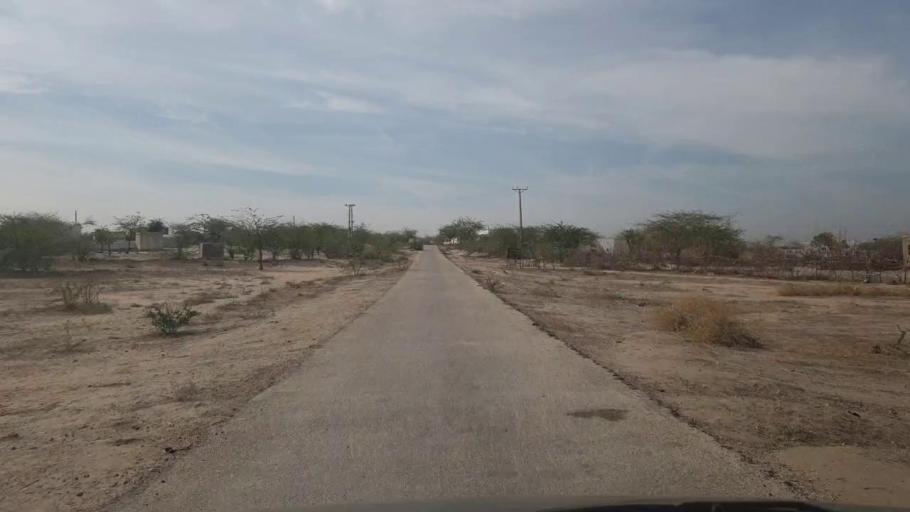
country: PK
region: Sindh
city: Umarkot
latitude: 25.2802
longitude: 69.7451
